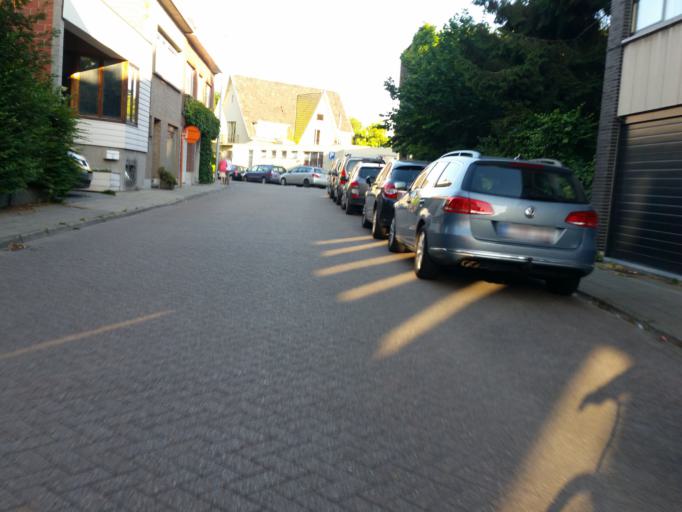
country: BE
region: Flanders
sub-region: Provincie Antwerpen
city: Mechelen
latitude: 51.0274
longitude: 4.4655
